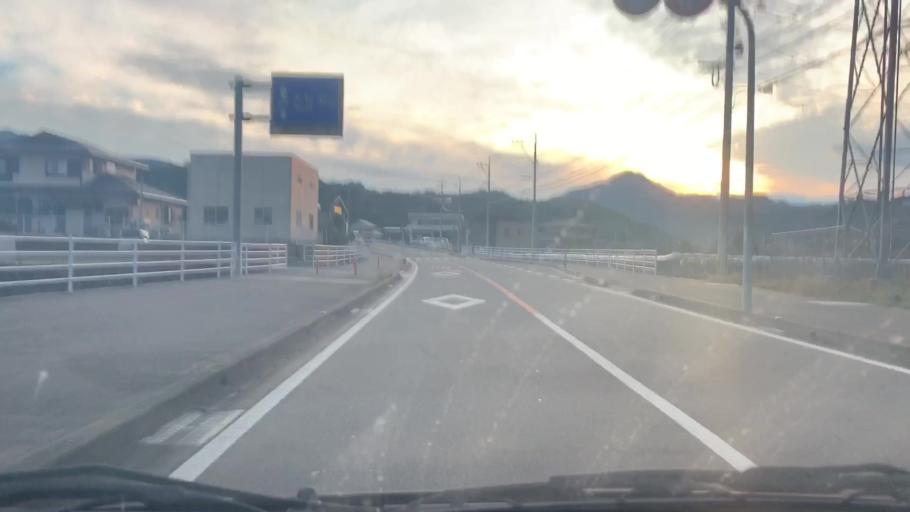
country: JP
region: Saga Prefecture
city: Kashima
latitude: 33.0923
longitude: 130.0888
